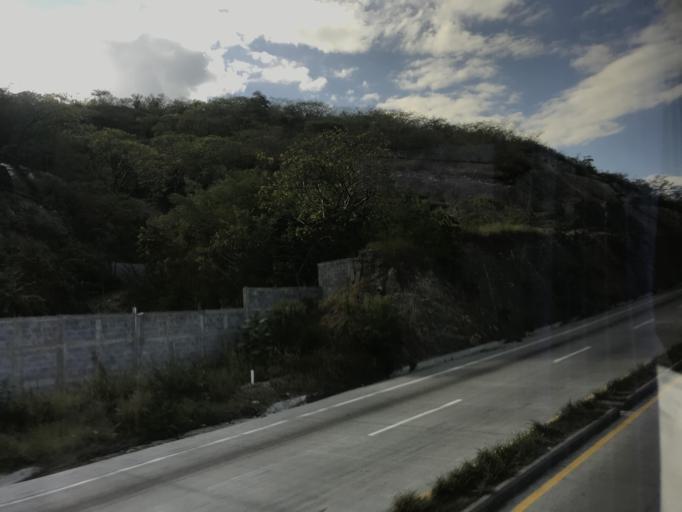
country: GT
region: El Progreso
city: Guastatoya
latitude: 14.8493
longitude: -90.1044
